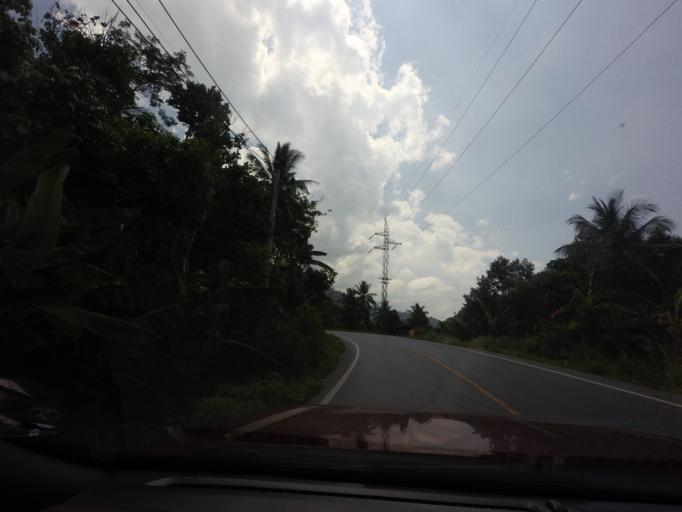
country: TH
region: Yala
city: Than To
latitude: 5.9874
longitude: 101.1938
